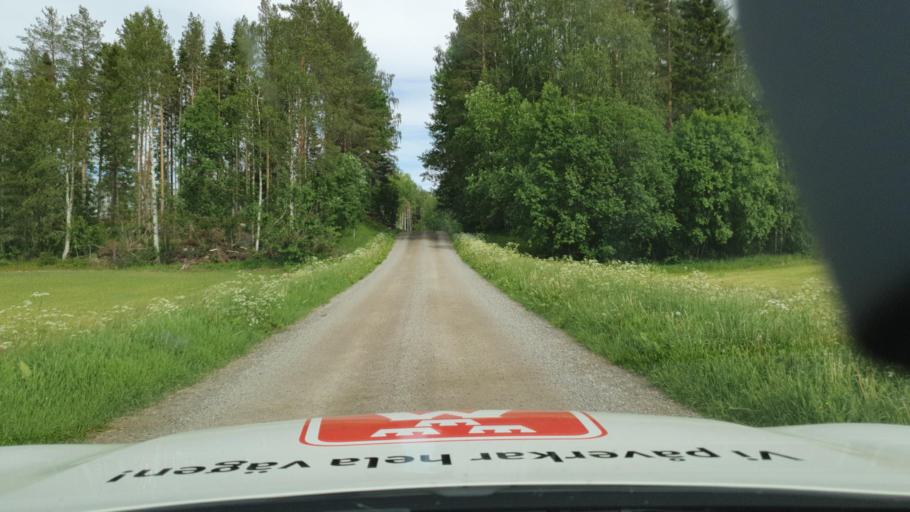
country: SE
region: Vaesterbotten
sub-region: Robertsfors Kommun
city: Robertsfors
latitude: 64.3731
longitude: 21.0489
